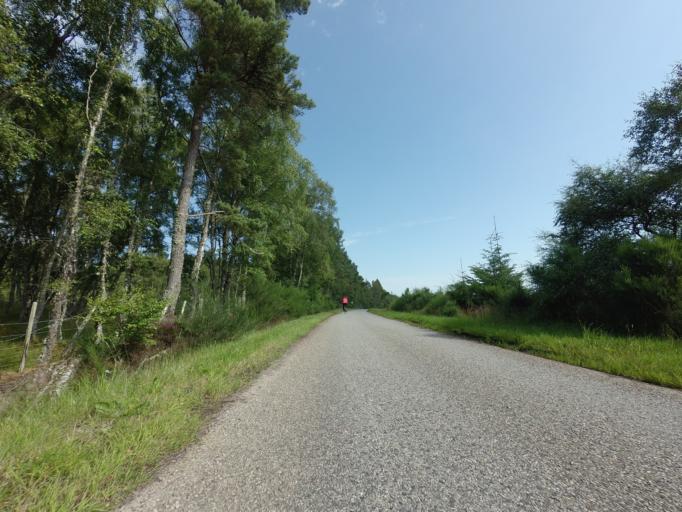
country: GB
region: Scotland
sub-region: Highland
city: Invergordon
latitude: 57.7343
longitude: -4.1907
